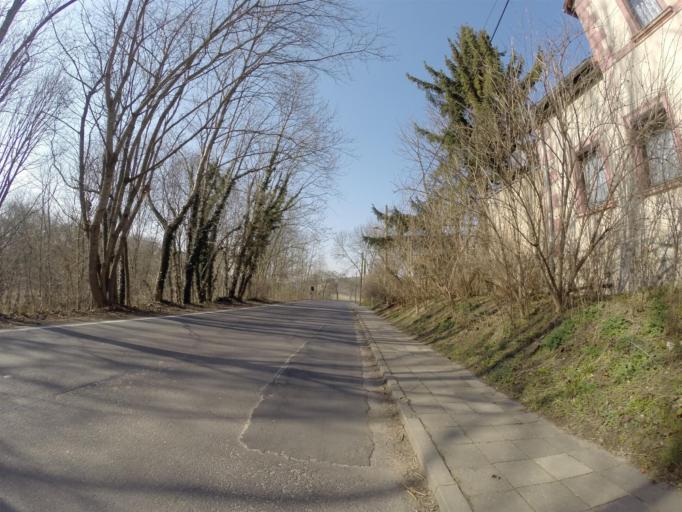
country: DE
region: Thuringia
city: Mellingen
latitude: 50.9511
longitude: 11.3759
